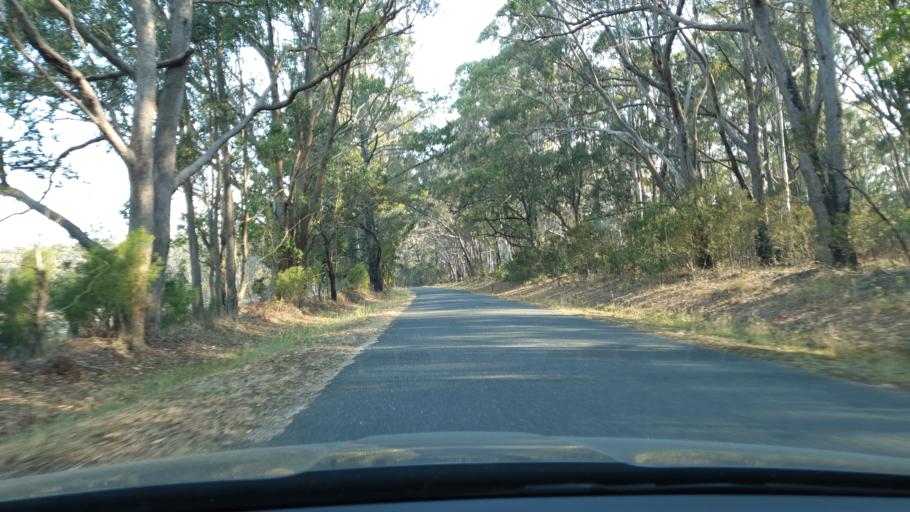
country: AU
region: New South Wales
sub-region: Tenterfield Municipality
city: Carrolls Creek
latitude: -28.6935
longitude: 152.0904
